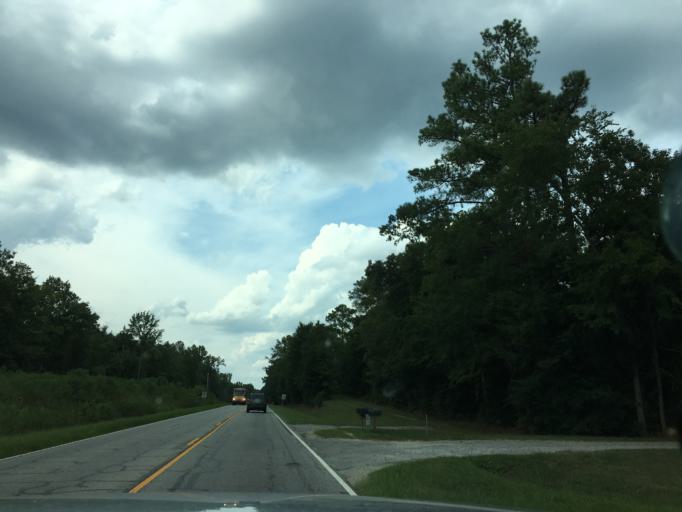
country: US
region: South Carolina
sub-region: Richland County
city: Lake Murray of Richland
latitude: 34.1537
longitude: -81.2481
